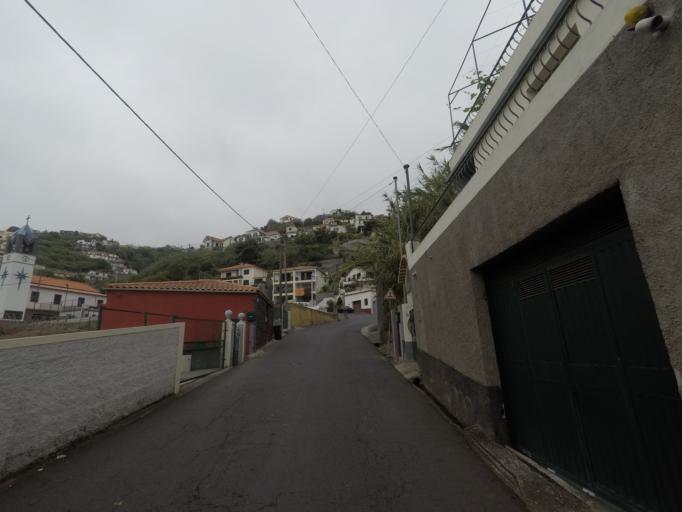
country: PT
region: Madeira
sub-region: Funchal
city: Nossa Senhora do Monte
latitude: 32.6743
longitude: -16.9404
